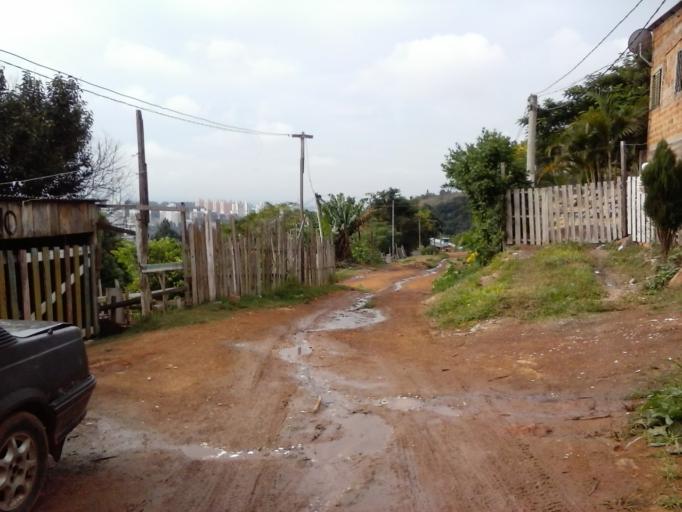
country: BR
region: Rio Grande do Sul
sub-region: Porto Alegre
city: Porto Alegre
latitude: -30.0595
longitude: -51.1412
